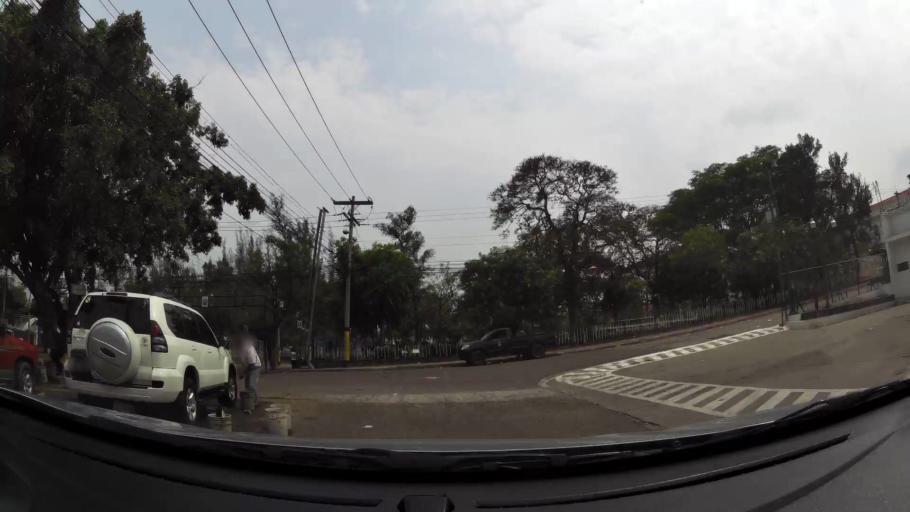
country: HN
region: Francisco Morazan
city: Tegucigalpa
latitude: 14.0920
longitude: -87.2079
